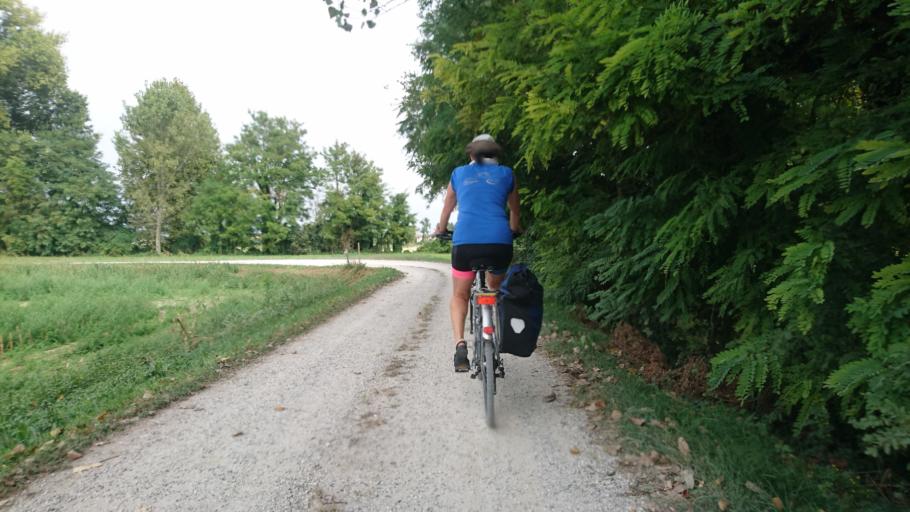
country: IT
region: Veneto
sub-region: Provincia di Padova
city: Grantorto
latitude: 45.5824
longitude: 11.7520
